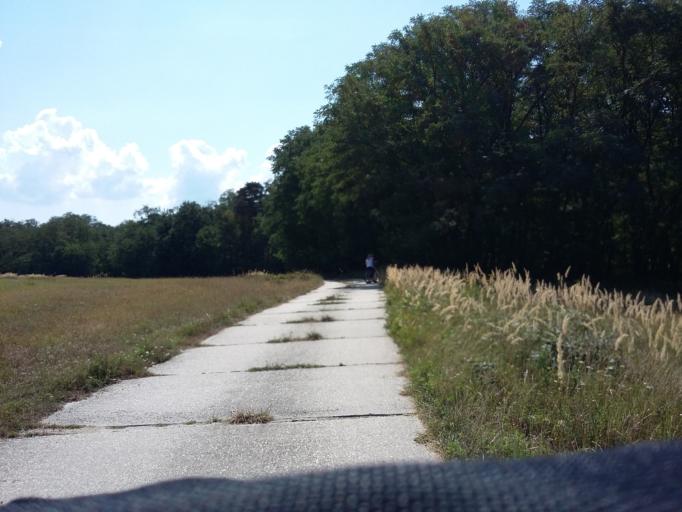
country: SK
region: Bratislavsky
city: Stupava
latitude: 48.3149
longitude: 17.0329
